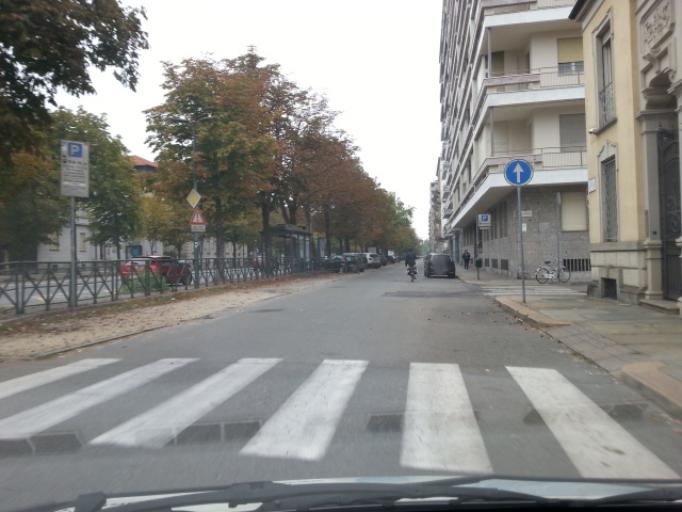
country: IT
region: Piedmont
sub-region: Provincia di Torino
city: Turin
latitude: 45.0585
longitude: 7.6663
